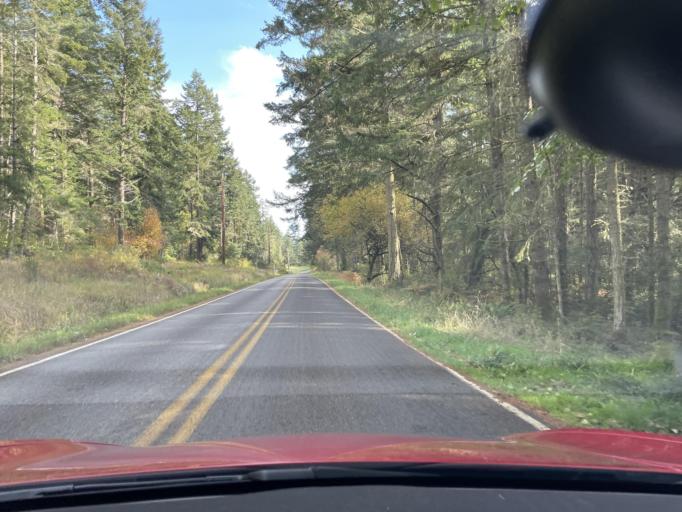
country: US
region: Washington
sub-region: San Juan County
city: Friday Harbor
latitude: 48.5185
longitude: -122.9933
